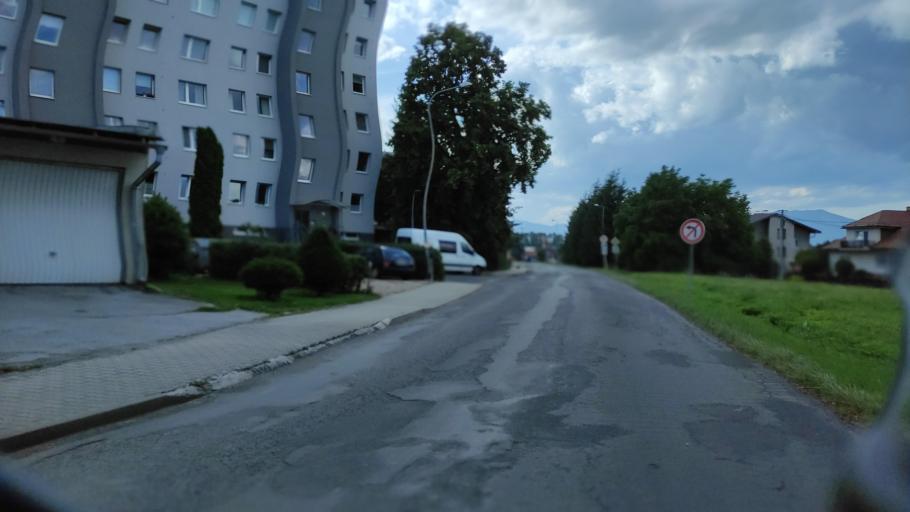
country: SK
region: Zilinsky
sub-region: Okres Liptovsky Mikulas
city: Liptovsky Mikulas
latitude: 49.0860
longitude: 19.5899
